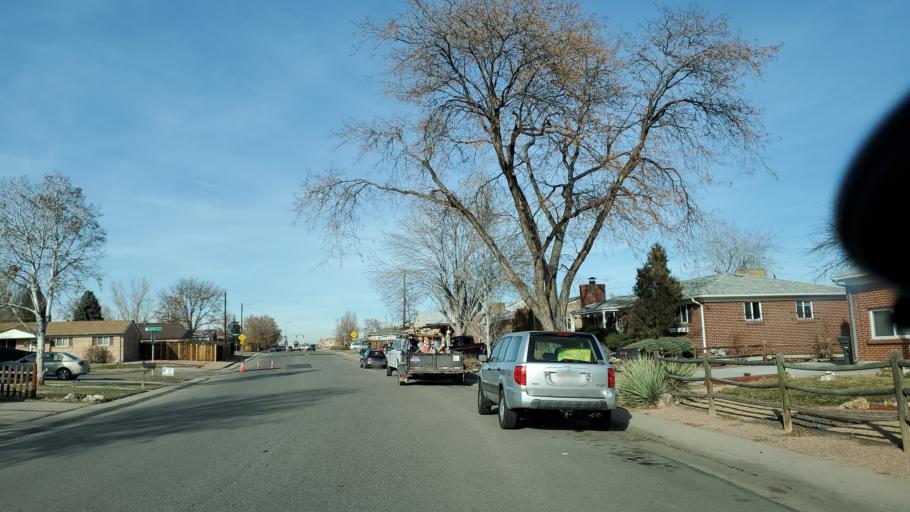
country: US
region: Colorado
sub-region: Adams County
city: Northglenn
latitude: 39.9109
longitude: -104.9596
